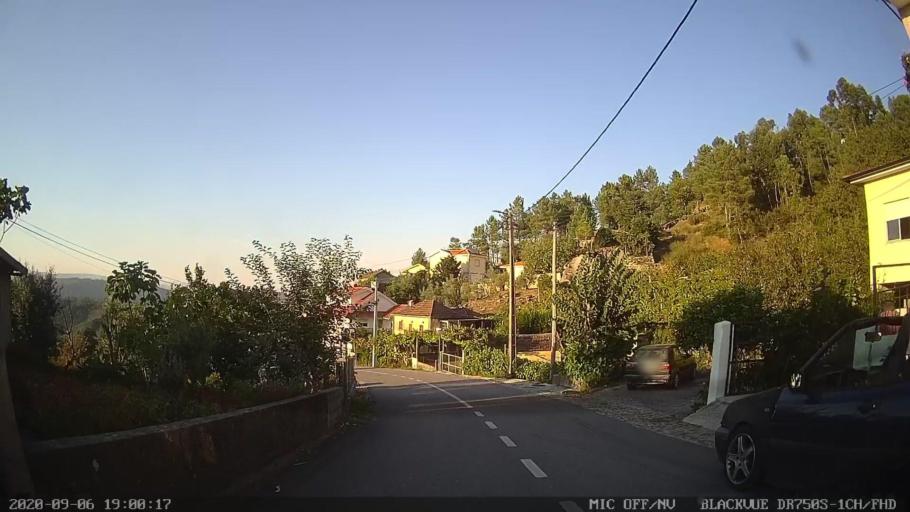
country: PT
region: Porto
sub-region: Baiao
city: Baiao
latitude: 41.2390
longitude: -7.9977
